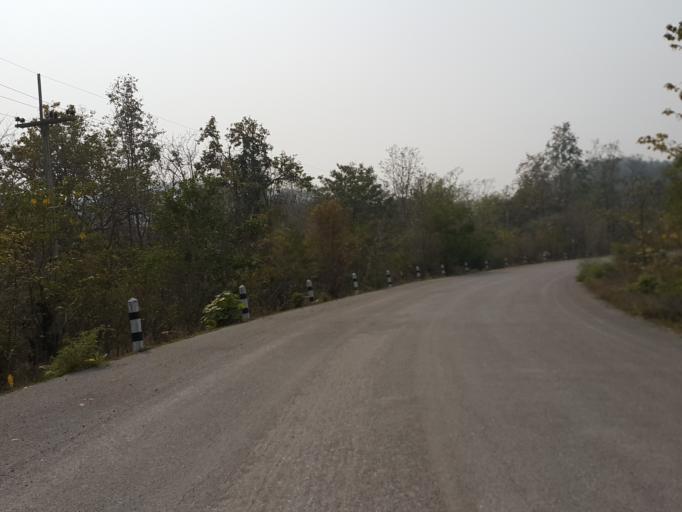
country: TH
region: Lampang
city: Mae Phrik
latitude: 17.5031
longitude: 99.0803
